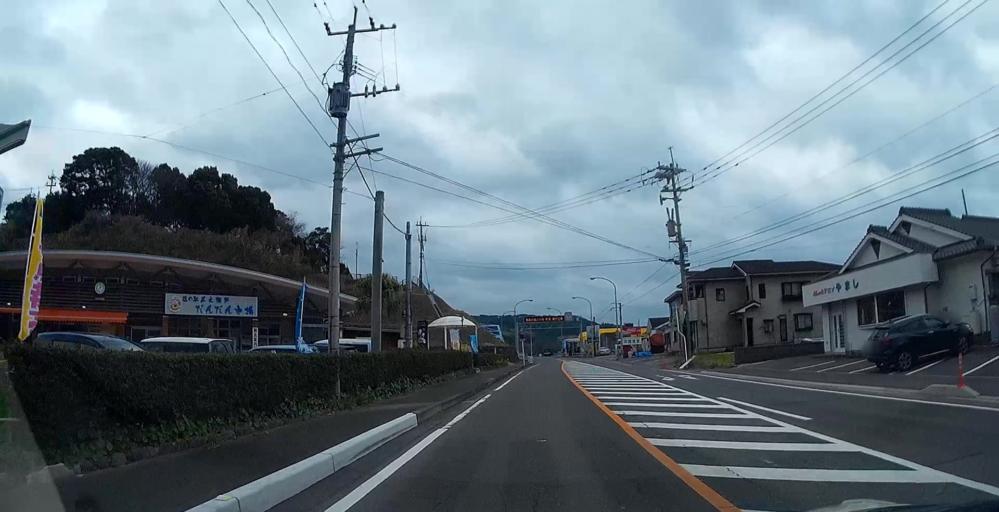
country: JP
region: Kagoshima
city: Akune
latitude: 32.1083
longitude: 130.1706
